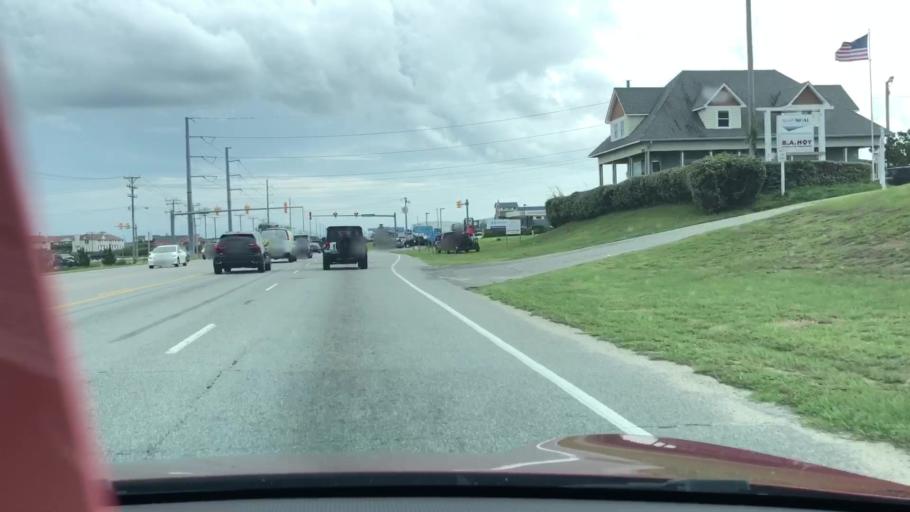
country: US
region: North Carolina
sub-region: Dare County
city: Kitty Hawk
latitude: 36.0675
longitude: -75.6943
